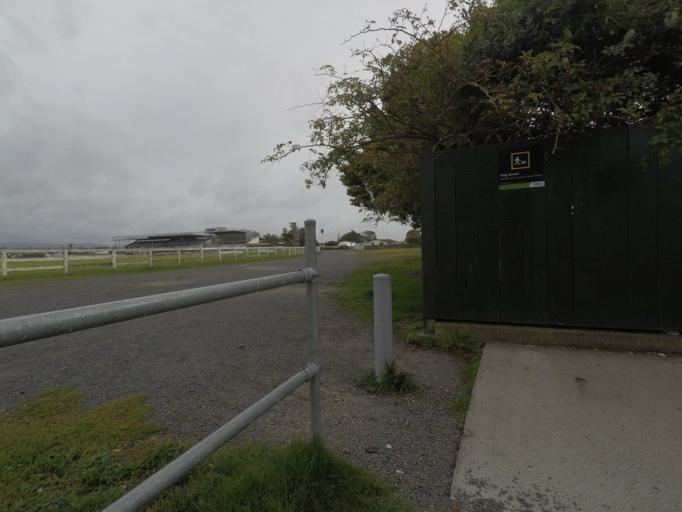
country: NZ
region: Auckland
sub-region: Auckland
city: Rosebank
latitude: -36.8964
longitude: 174.6944
